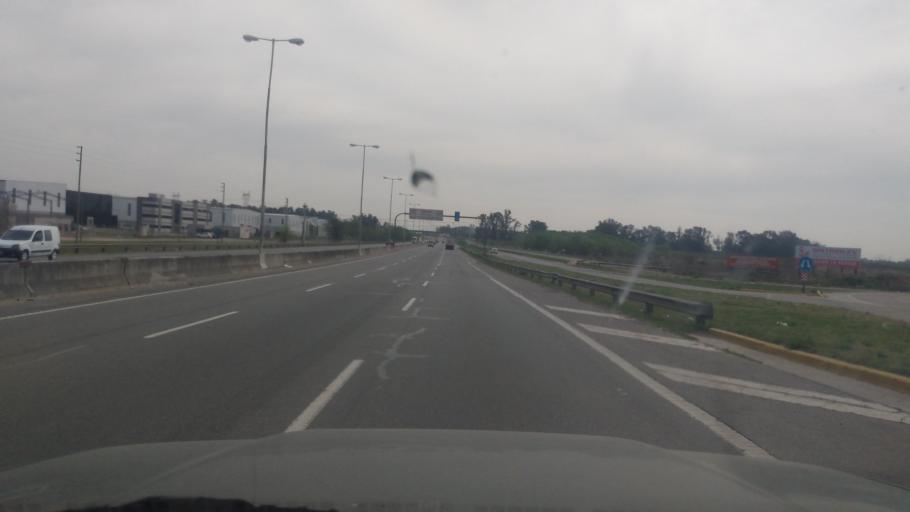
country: AR
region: Buenos Aires
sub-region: Partido de Pilar
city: Pilar
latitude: -34.4107
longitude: -59.0056
